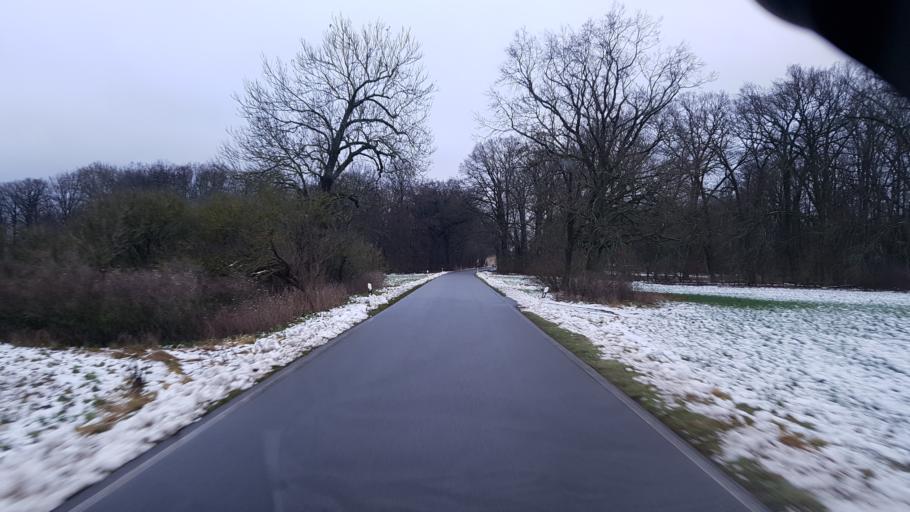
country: DE
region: Brandenburg
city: Luckau
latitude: 51.7989
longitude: 13.7346
